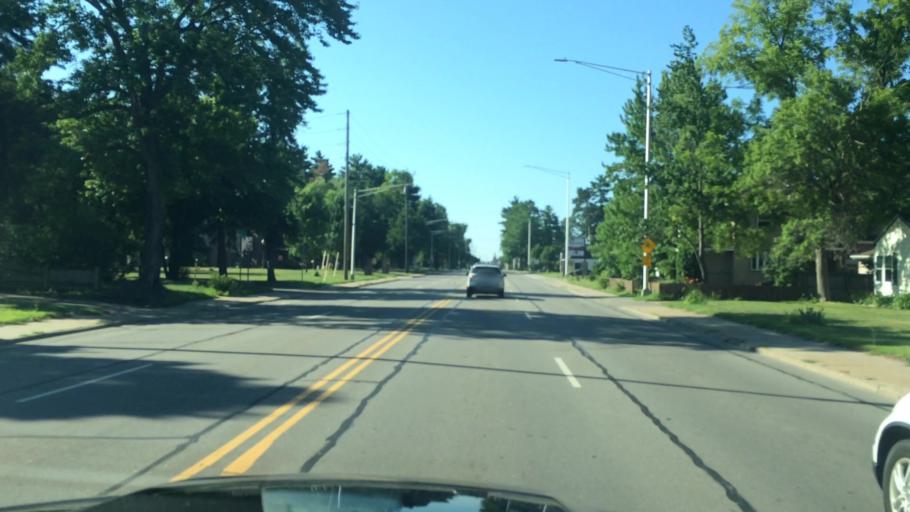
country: US
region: Wisconsin
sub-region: Marathon County
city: Wausau
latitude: 44.9428
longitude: -89.6197
